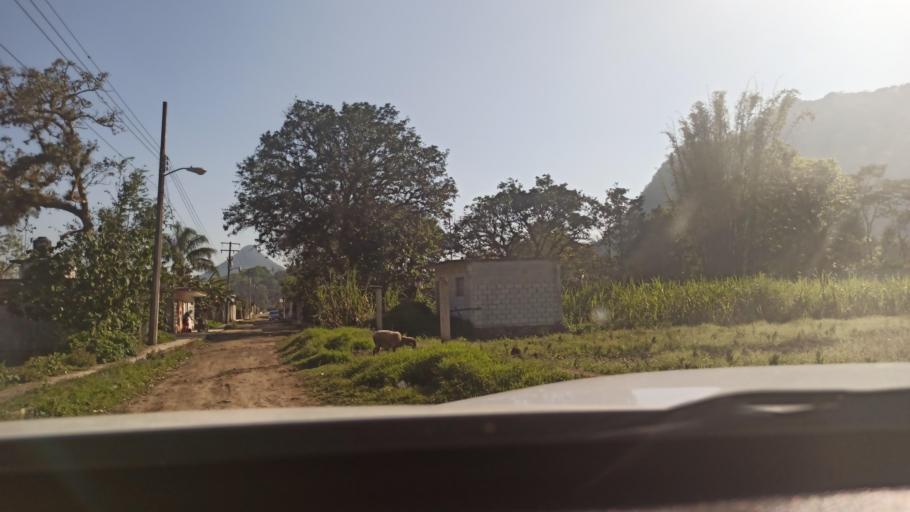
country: MX
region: Veracruz
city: Atzacan
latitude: 18.9119
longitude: -97.0867
